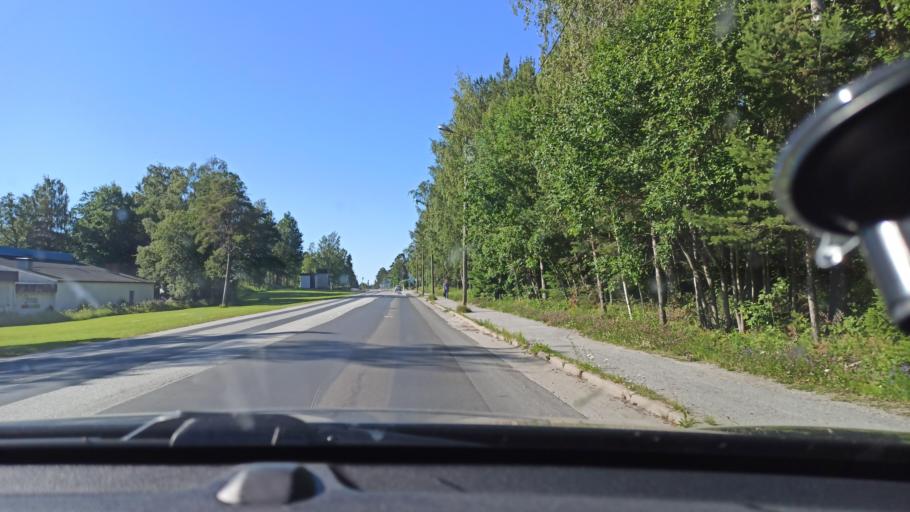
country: FI
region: Ostrobothnia
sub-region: Jakobstadsregionen
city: Jakobstad
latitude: 63.6792
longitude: 22.7187
